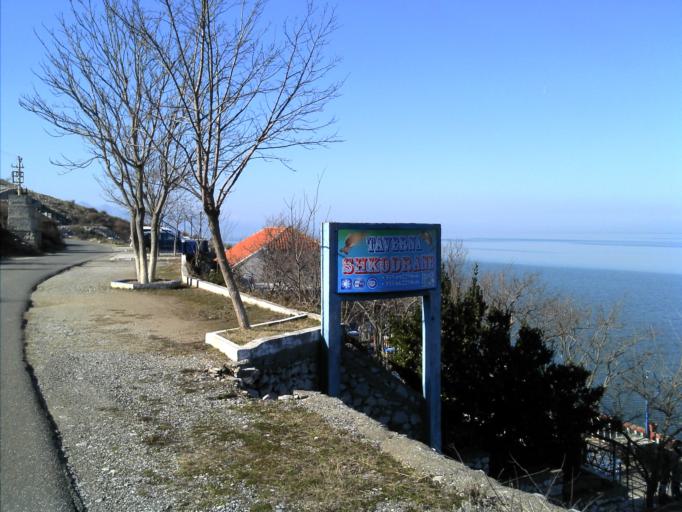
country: AL
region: Shkoder
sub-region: Rrethi i Shkodres
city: Berdica e Madhe
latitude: 42.0667
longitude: 19.4289
